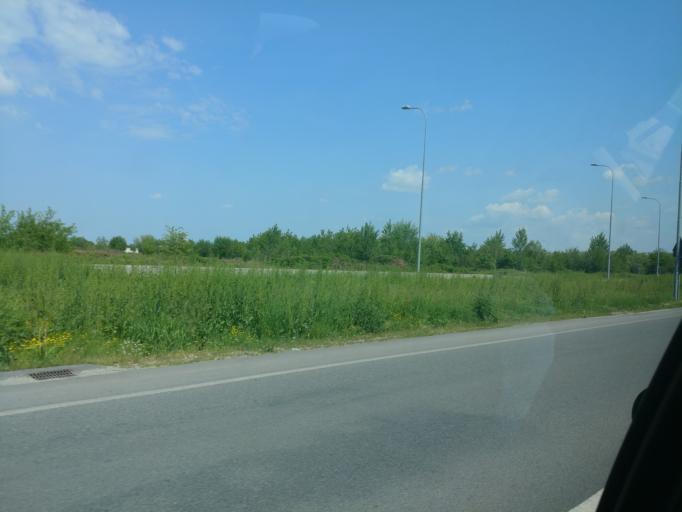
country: IT
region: Piedmont
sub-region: Provincia di Cuneo
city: Carde
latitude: 44.7354
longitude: 7.4202
